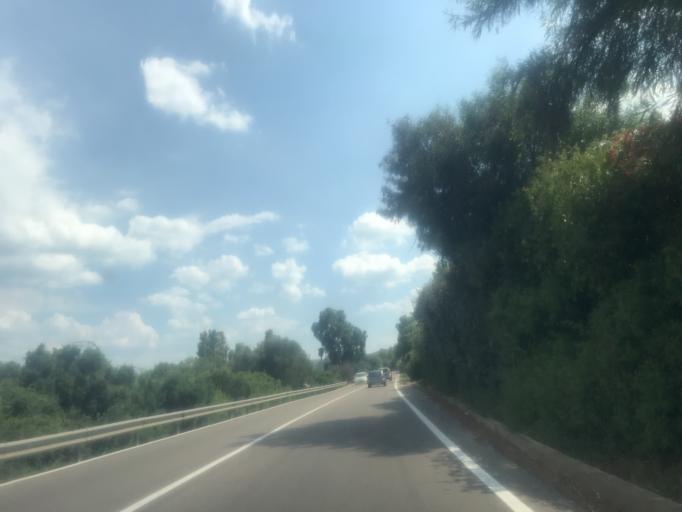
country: IT
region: Sardinia
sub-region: Provincia di Olbia-Tempio
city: San Teodoro
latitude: 40.8664
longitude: 9.6415
